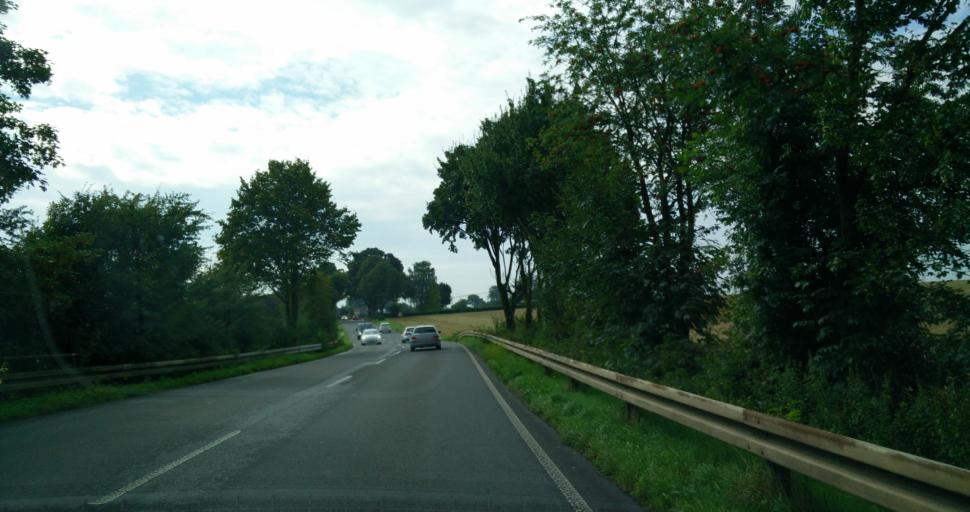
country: DE
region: North Rhine-Westphalia
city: Wulfrath
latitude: 51.2497
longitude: 7.0256
